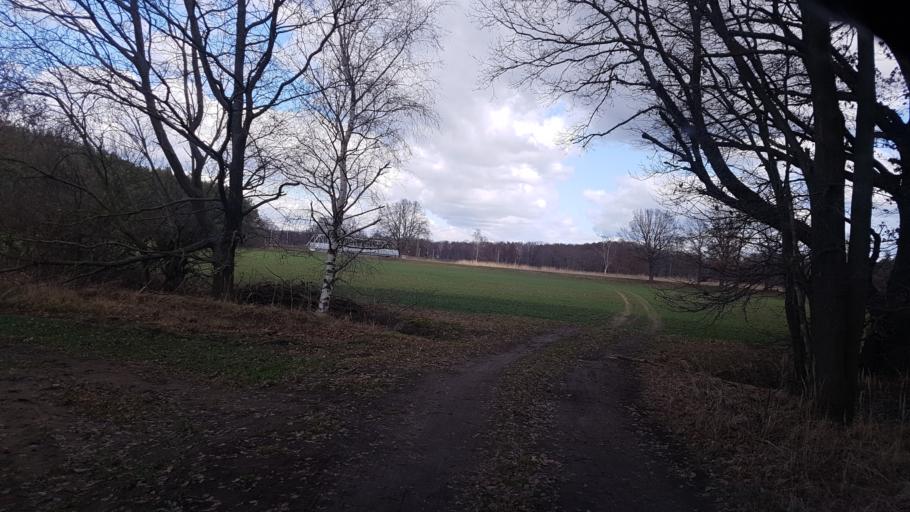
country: DE
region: Brandenburg
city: Schilda
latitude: 51.5853
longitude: 13.3306
